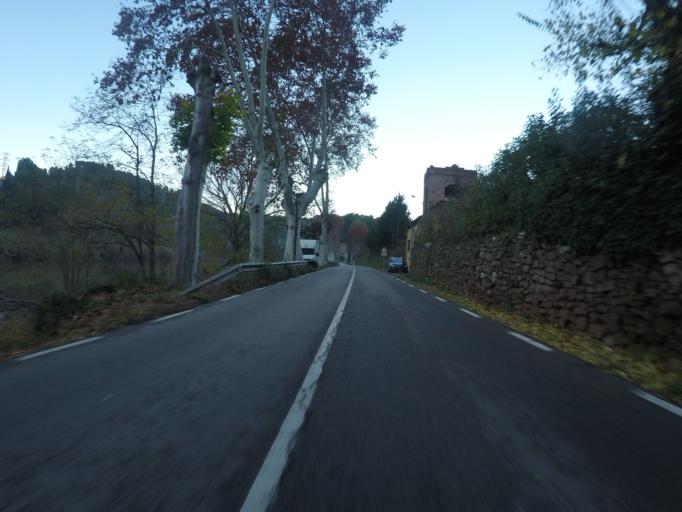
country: ES
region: Catalonia
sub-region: Provincia de Barcelona
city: Monistrol de Montserrat
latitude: 41.6165
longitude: 1.8523
